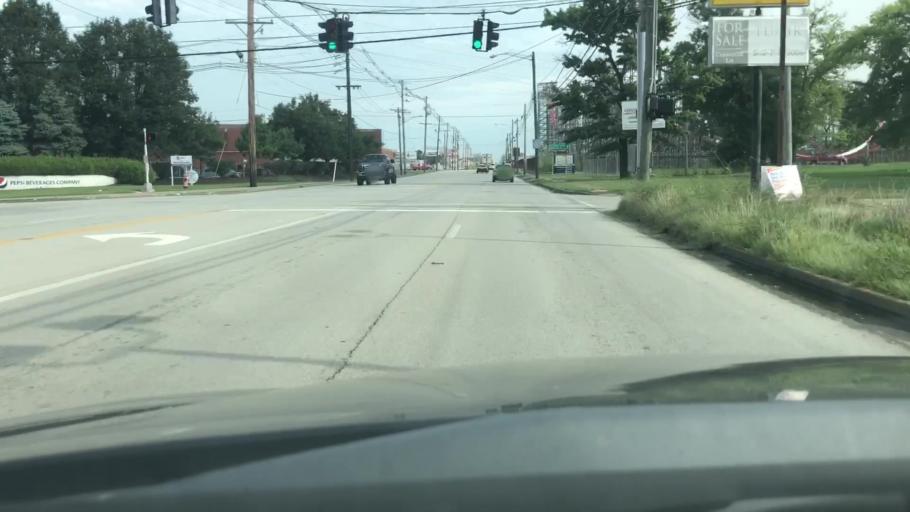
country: US
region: Kentucky
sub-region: Jefferson County
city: Audubon Park
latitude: 38.1938
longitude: -85.7509
